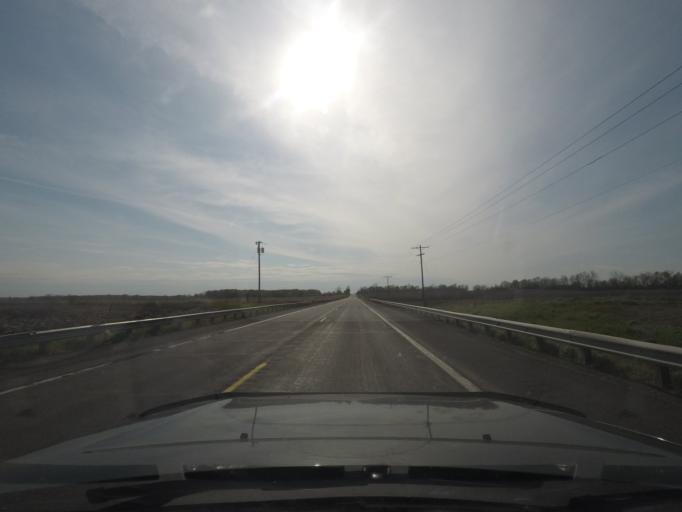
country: US
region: Michigan
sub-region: Berrien County
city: Three Oaks
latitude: 41.7984
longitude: -86.5605
